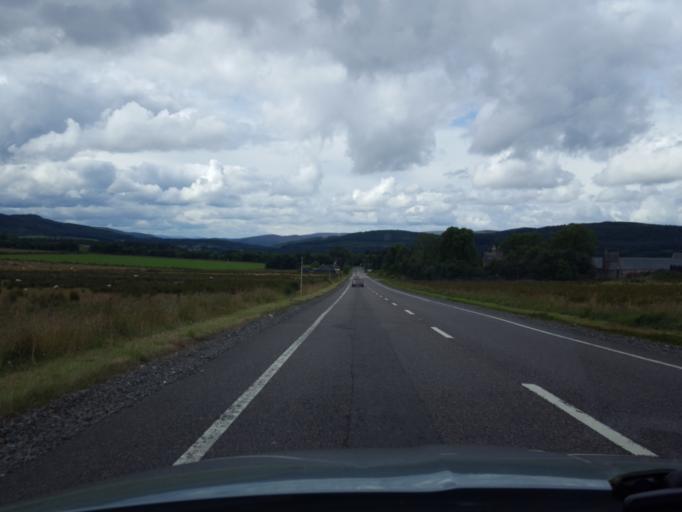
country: GB
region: Scotland
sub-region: Moray
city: Rothes
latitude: 57.4315
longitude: -3.3310
